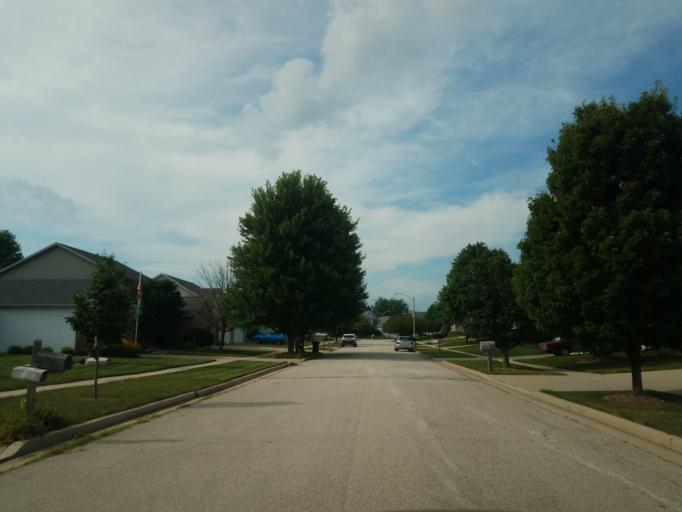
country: US
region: Illinois
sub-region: McLean County
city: Normal
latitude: 40.5009
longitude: -88.9128
